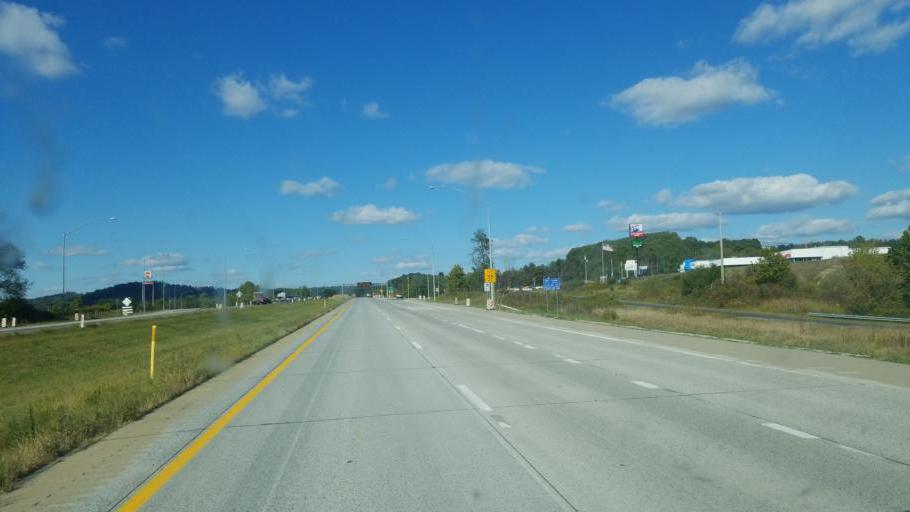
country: US
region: West Virginia
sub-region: Monongalia County
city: Star City
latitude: 39.7290
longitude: -80.0594
